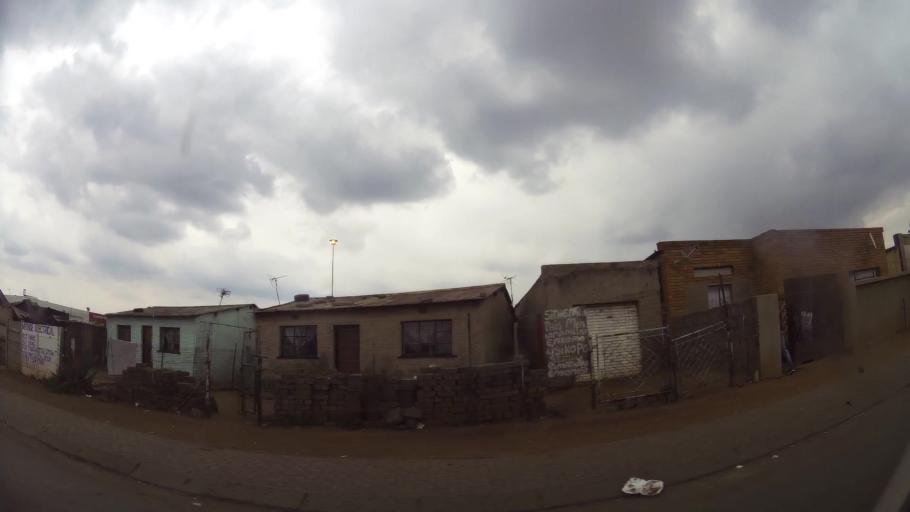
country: ZA
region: Gauteng
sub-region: Ekurhuleni Metropolitan Municipality
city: Germiston
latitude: -26.3420
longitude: 28.1497
